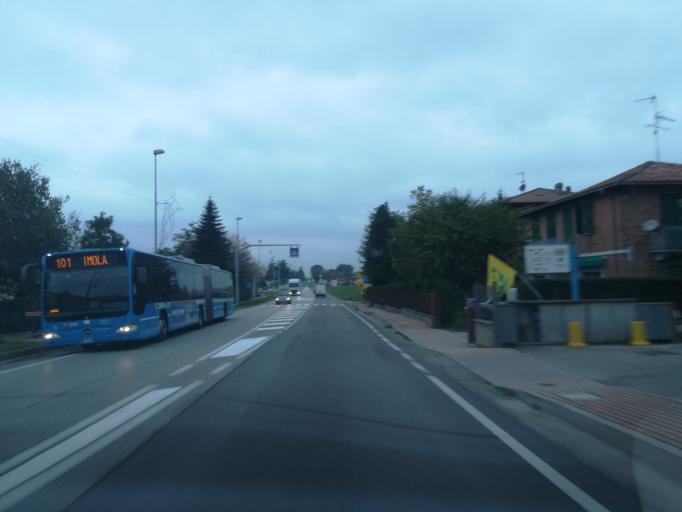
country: IT
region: Emilia-Romagna
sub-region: Provincia di Bologna
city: Toscanella
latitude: 44.3845
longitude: 11.6342
